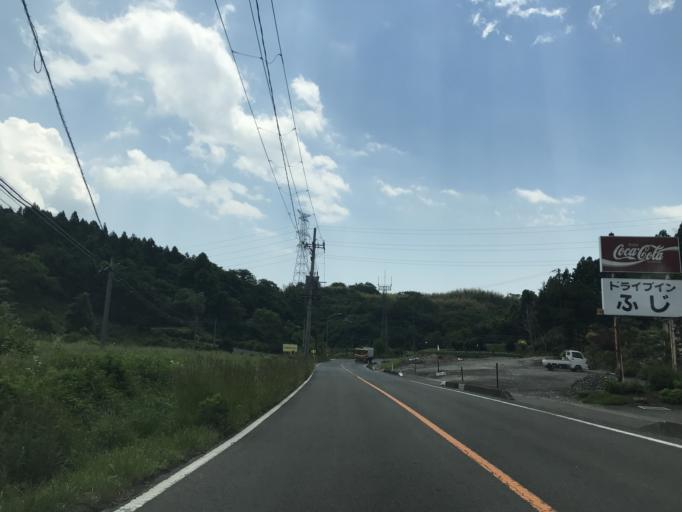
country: JP
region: Miyagi
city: Matsushima
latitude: 38.4157
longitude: 141.0625
